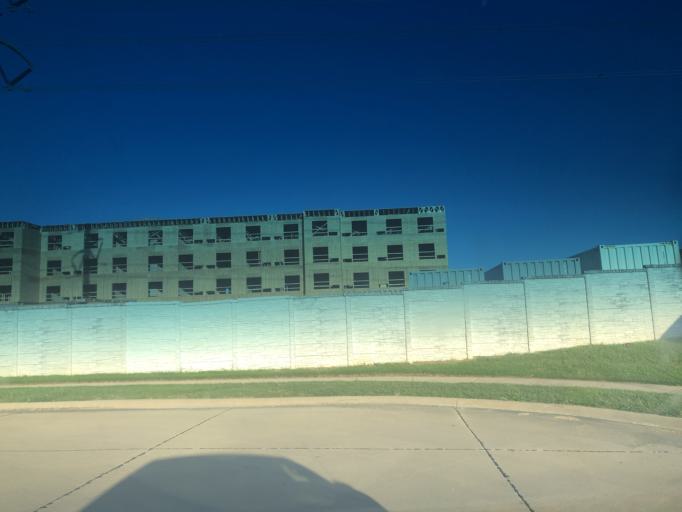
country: US
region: Texas
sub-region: Dallas County
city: Grand Prairie
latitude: 32.7041
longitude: -97.0220
